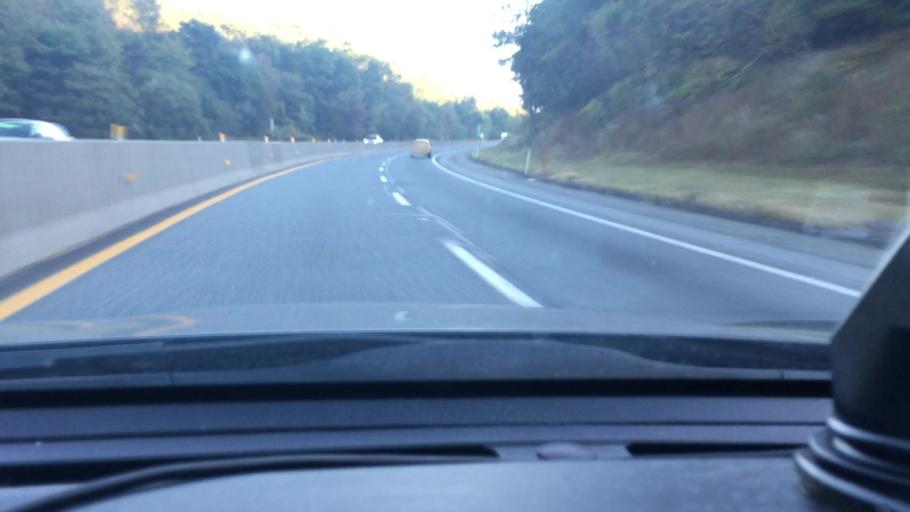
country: US
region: Pennsylvania
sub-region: Carbon County
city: Weissport East
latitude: 40.9186
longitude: -75.6483
